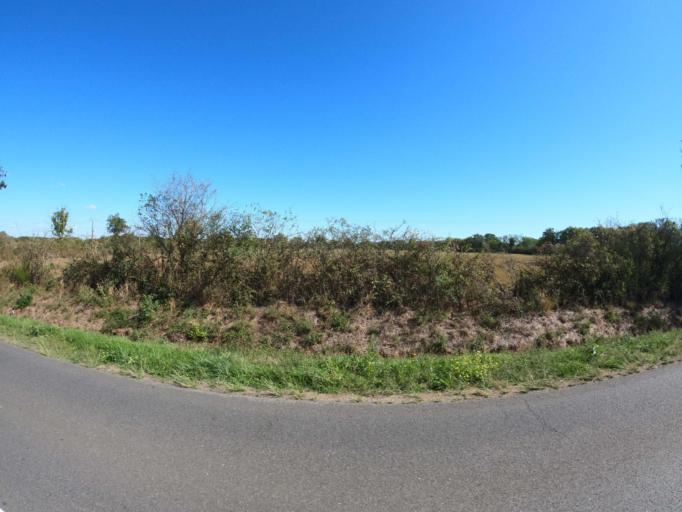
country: FR
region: Poitou-Charentes
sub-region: Departement de la Vienne
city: Lathus-Saint-Remy
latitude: 46.3618
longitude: 0.9415
